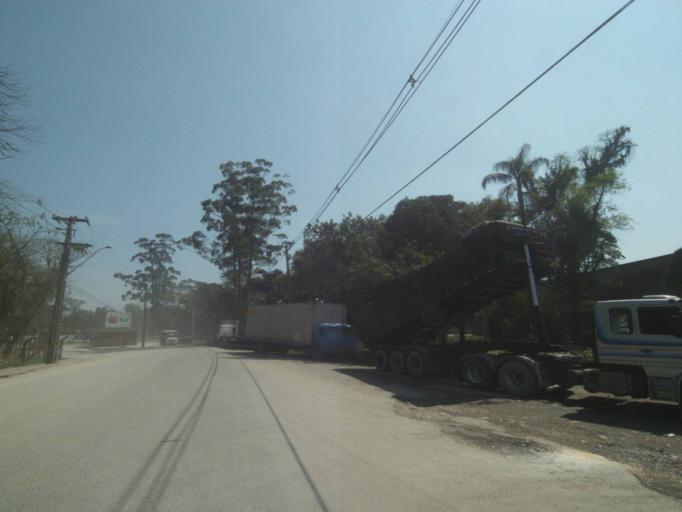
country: BR
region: Parana
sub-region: Paranagua
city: Paranagua
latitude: -25.5463
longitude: -48.5632
